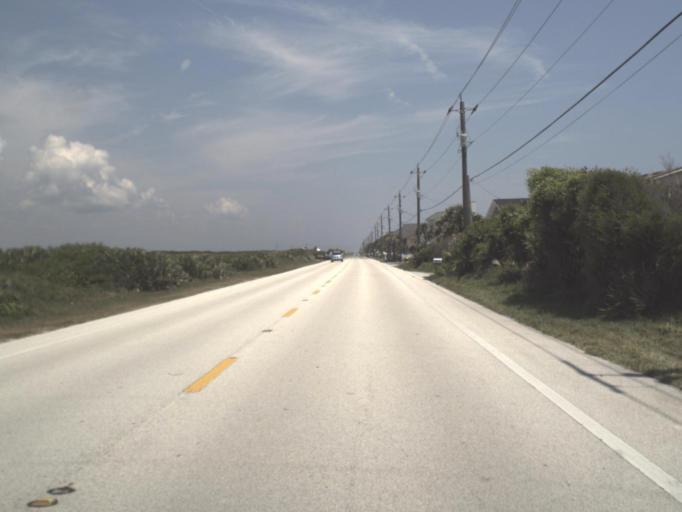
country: US
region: Florida
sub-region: Saint Johns County
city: Villano Beach
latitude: 30.0134
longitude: -81.3209
